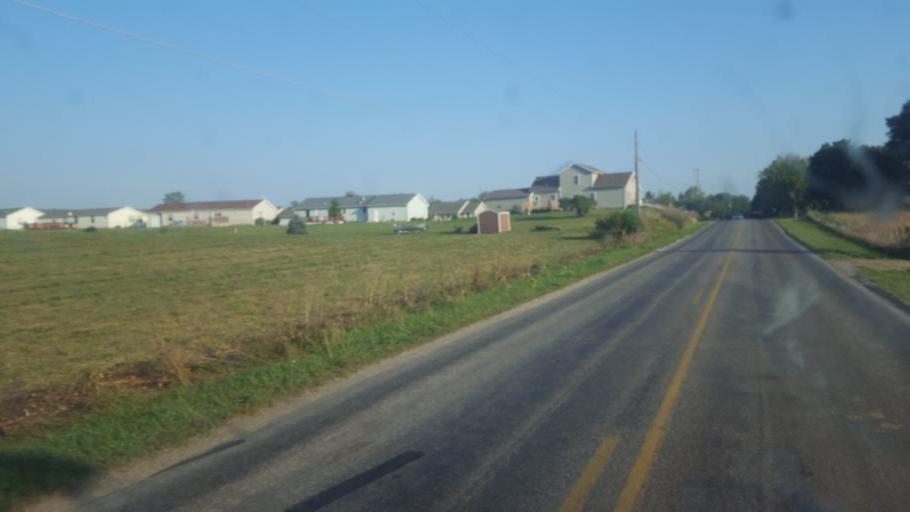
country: US
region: Indiana
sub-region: LaGrange County
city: Lagrange
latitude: 41.6312
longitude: -85.4247
